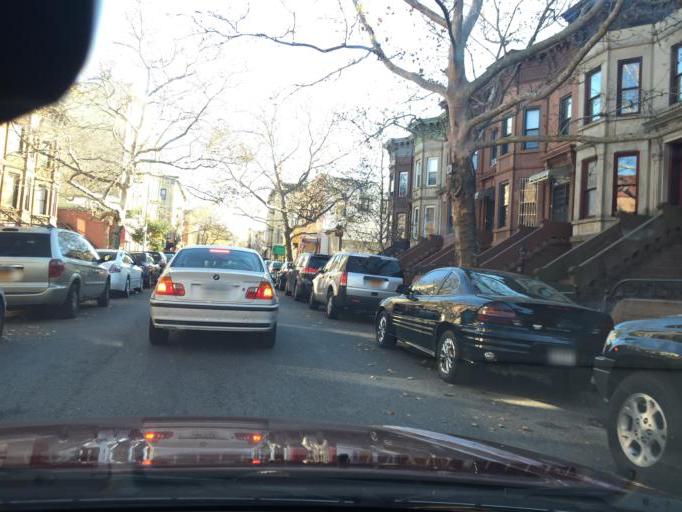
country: US
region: New York
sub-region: Kings County
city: Bensonhurst
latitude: 40.6423
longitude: -74.0148
